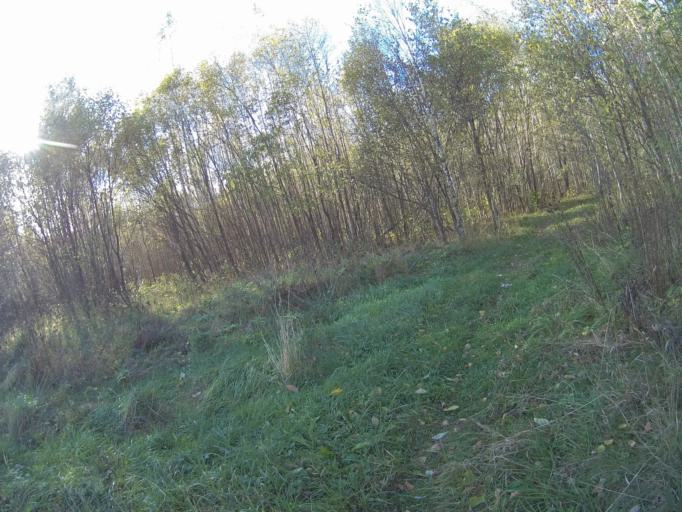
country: RU
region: Vladimir
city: Golovino
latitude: 56.0003
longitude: 40.4979
